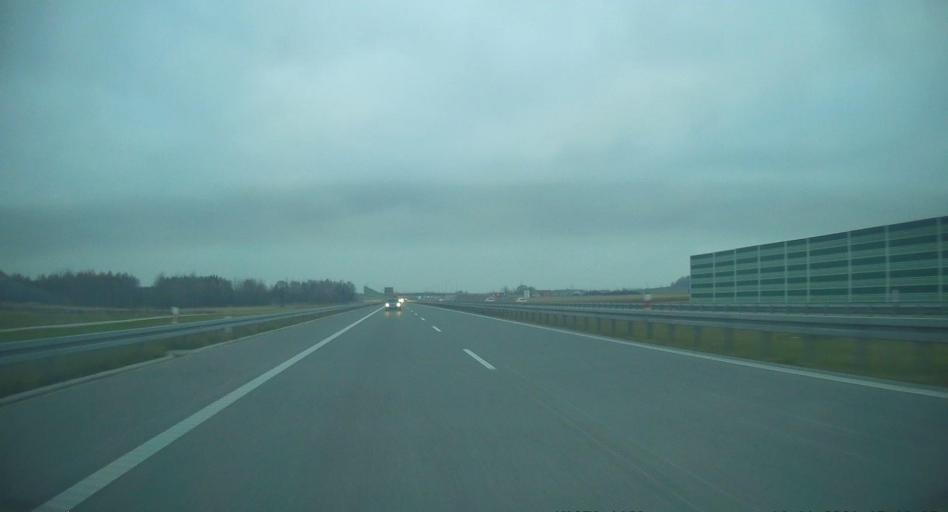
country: PL
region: Silesian Voivodeship
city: Wozniki
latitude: 50.5939
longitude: 19.0400
